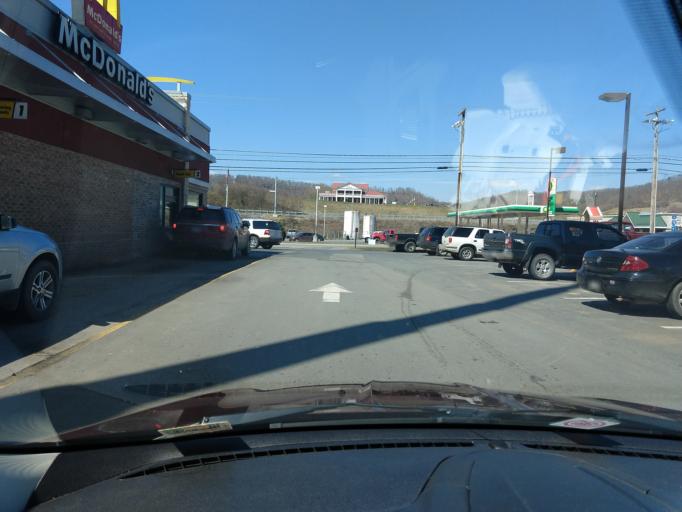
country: US
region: West Virginia
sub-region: Braxton County
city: Sutton
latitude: 38.6999
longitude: -80.6637
